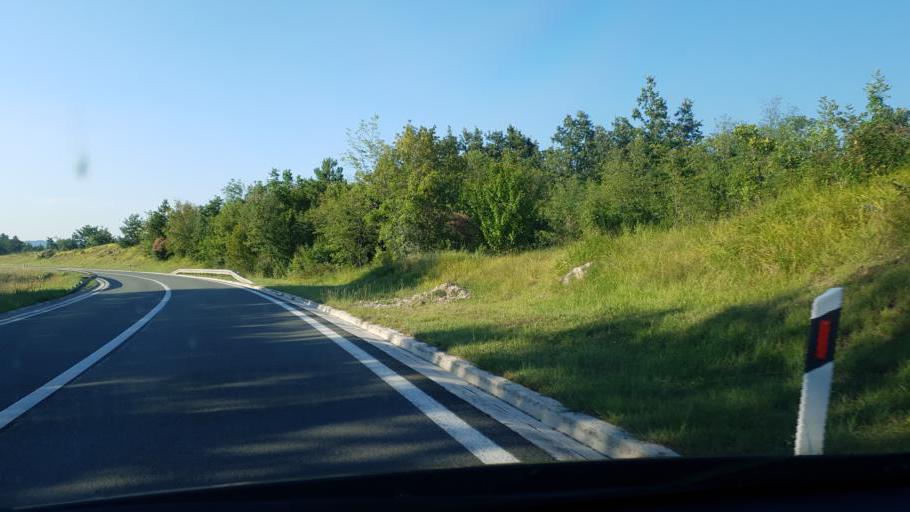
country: HR
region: Istarska
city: Buzet
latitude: 45.3249
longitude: 14.0759
